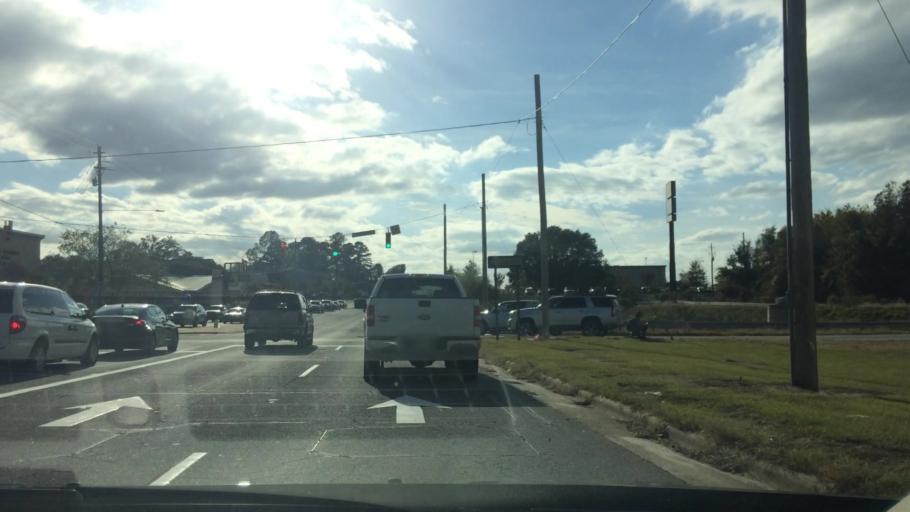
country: US
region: North Carolina
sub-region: Wayne County
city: Elroy
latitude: 35.3781
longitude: -77.9371
